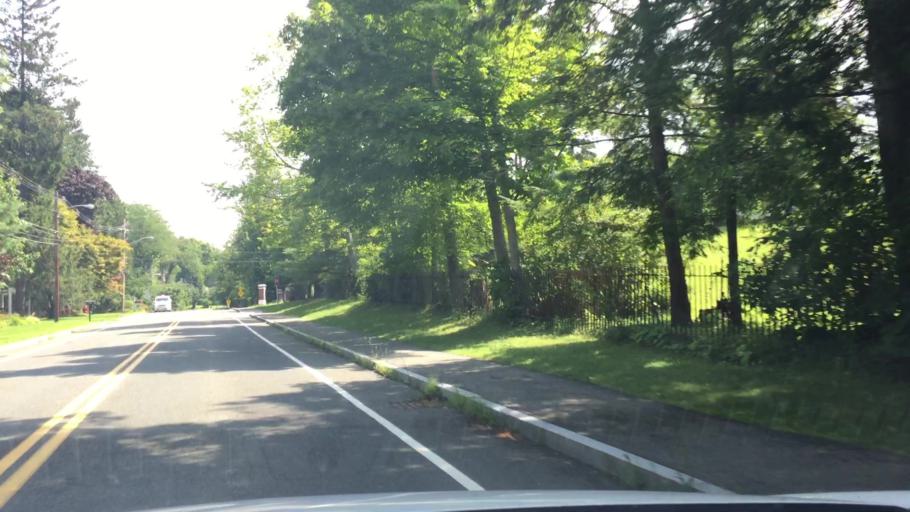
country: US
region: Massachusetts
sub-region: Berkshire County
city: Lenox
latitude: 42.3564
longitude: -73.2976
